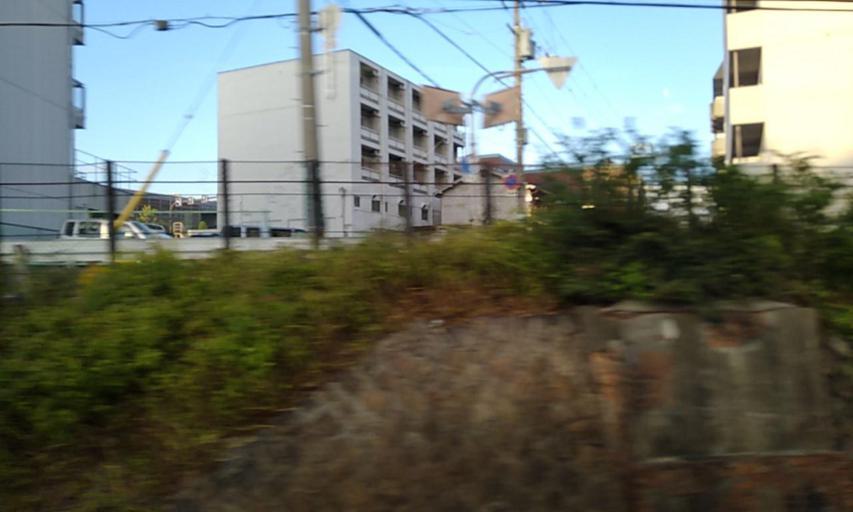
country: JP
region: Osaka
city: Sakai
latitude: 34.5675
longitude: 135.4898
